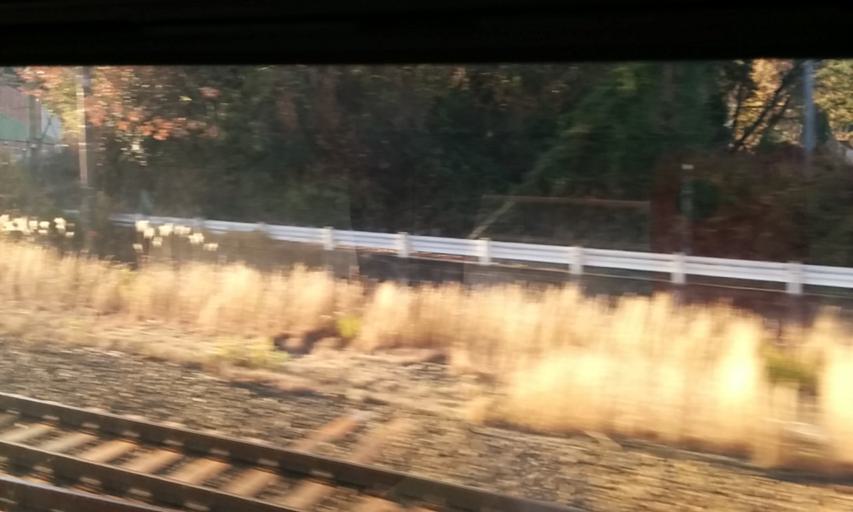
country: JP
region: Gifu
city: Mizunami
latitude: 35.4125
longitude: 137.3066
